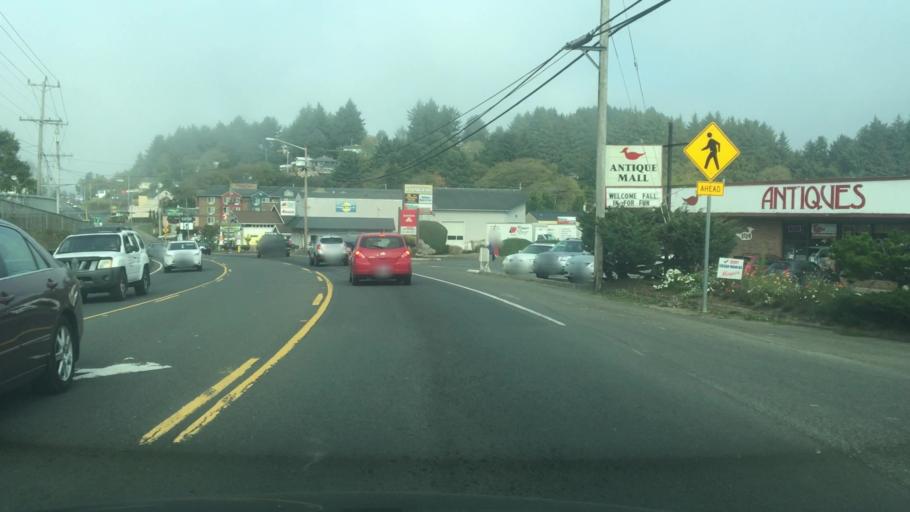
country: US
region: Oregon
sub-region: Lincoln County
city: Lincoln City
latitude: 44.9878
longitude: -124.0055
